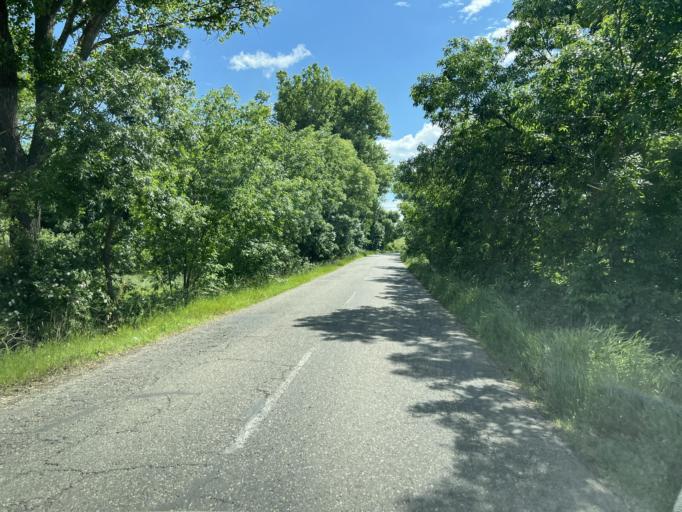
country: HU
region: Pest
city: Zsambok
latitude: 47.5517
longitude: 19.5933
